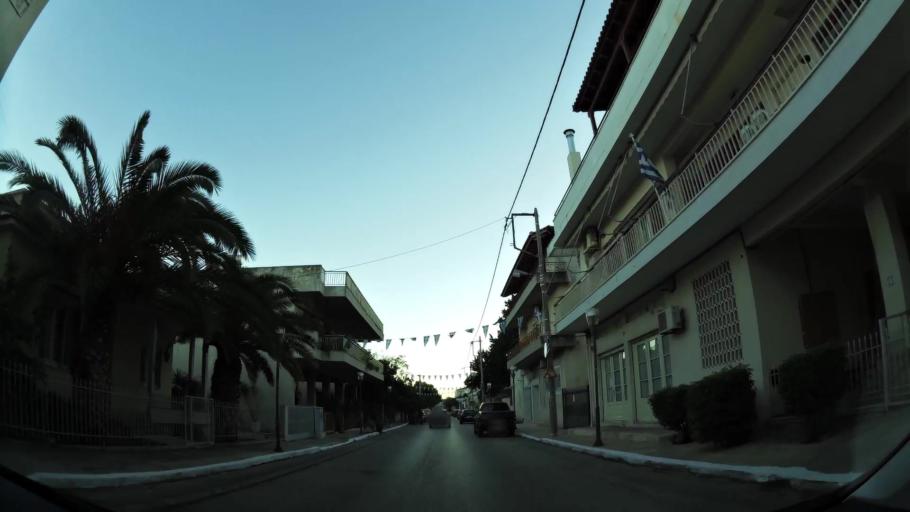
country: GR
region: Attica
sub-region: Nomarchia Anatolikis Attikis
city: Paiania
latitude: 37.9556
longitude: 23.8528
